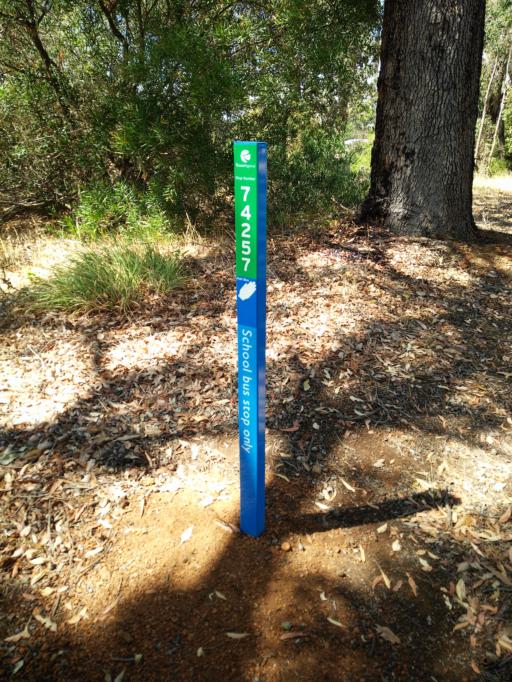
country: AU
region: Western Australia
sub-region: Bridgetown-Greenbushes
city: Bridgetown
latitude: -33.9590
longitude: 116.1531
